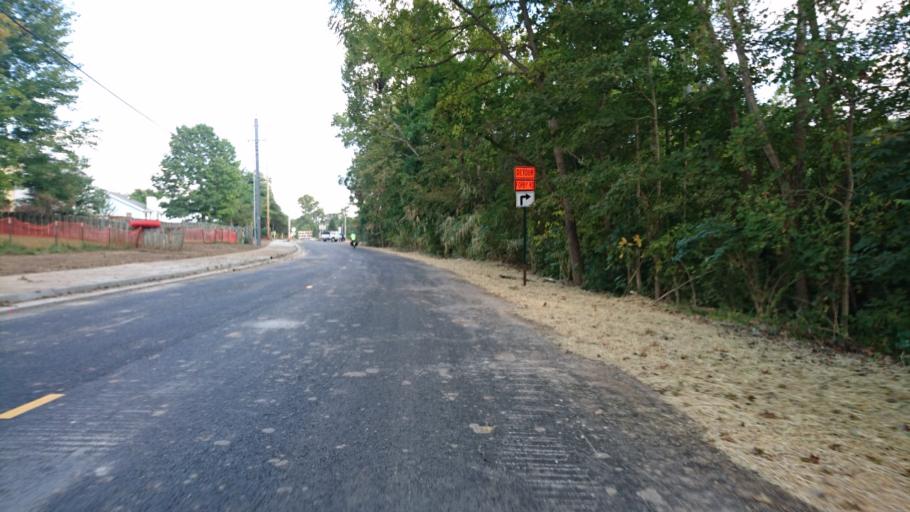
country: US
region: Missouri
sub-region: Saint Louis County
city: Eureka
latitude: 38.5170
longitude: -90.6428
